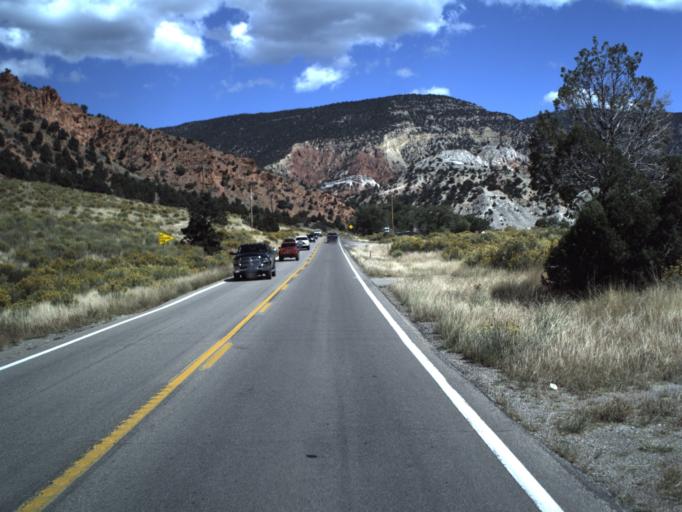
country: US
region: Utah
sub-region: Iron County
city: Cedar City
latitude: 37.6722
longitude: -113.0369
